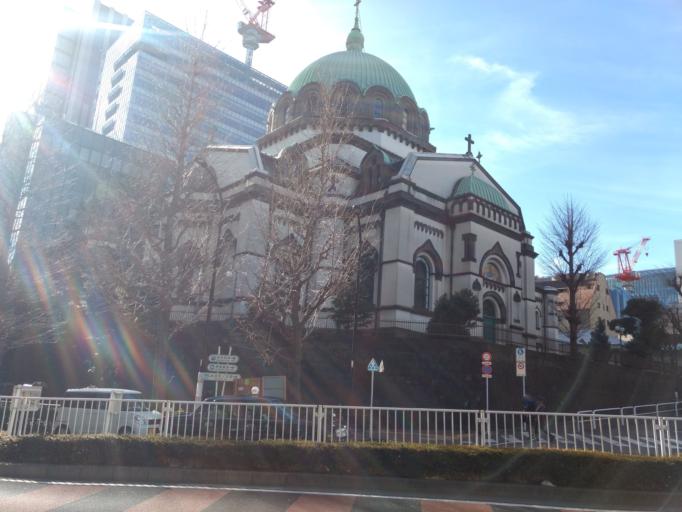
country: JP
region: Tokyo
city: Tokyo
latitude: 35.6982
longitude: 139.7659
